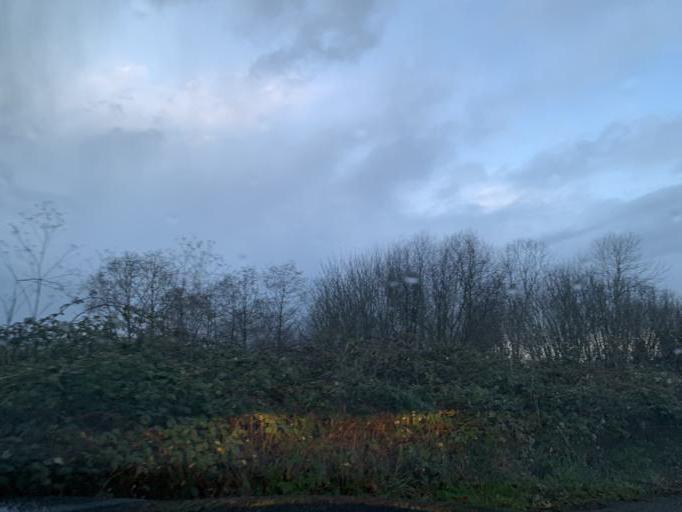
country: US
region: Washington
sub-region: King County
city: Seattle
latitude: 47.5707
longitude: -122.3167
